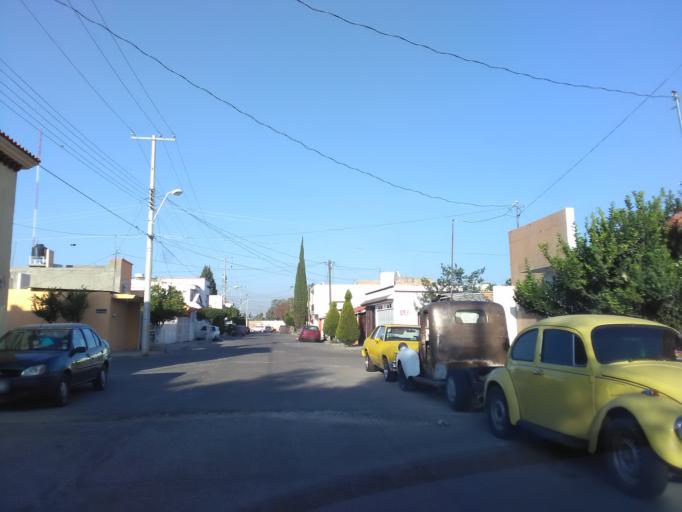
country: MX
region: Durango
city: Victoria de Durango
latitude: 24.0541
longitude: -104.6261
